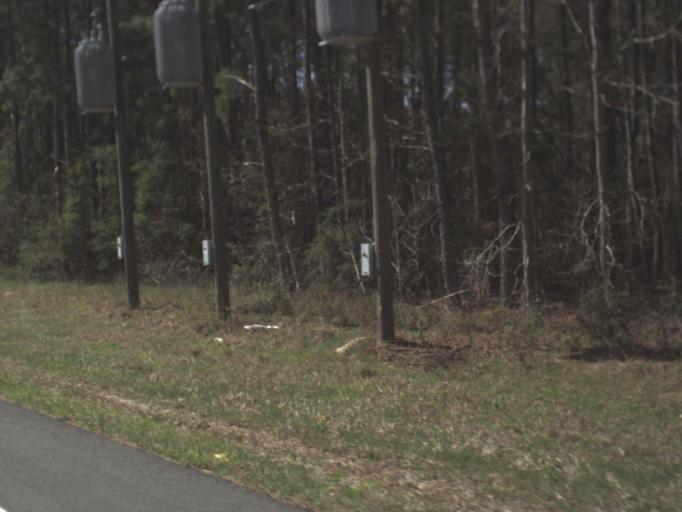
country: US
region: Florida
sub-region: Jefferson County
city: Monticello
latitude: 30.4667
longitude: -84.0196
